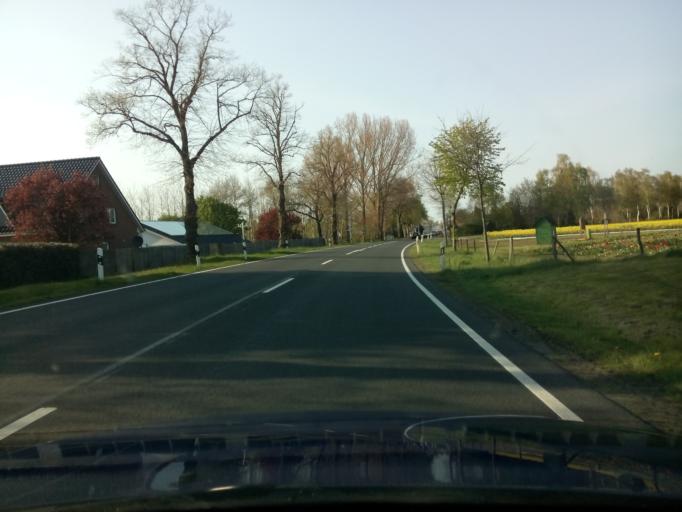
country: DE
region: Lower Saxony
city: Stuhr
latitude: 52.9830
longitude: 8.7871
